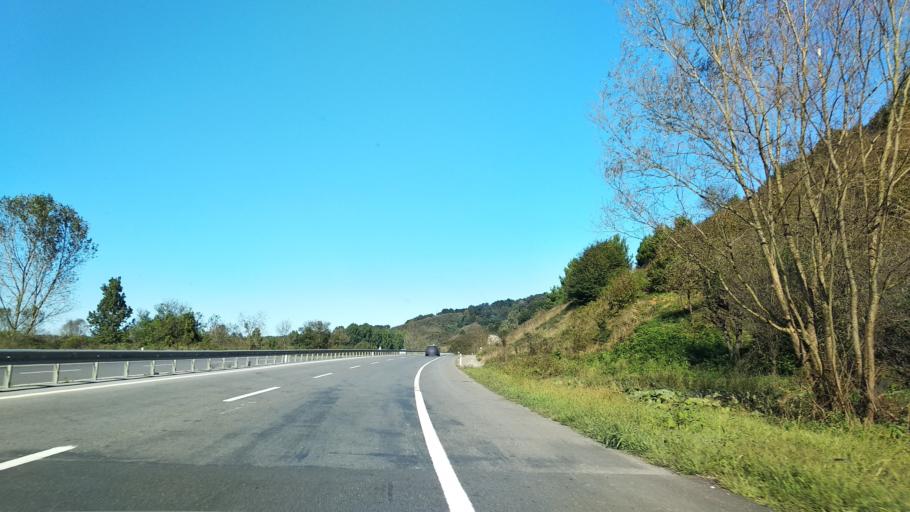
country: TR
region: Sakarya
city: Karasu
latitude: 41.0616
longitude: 30.6381
